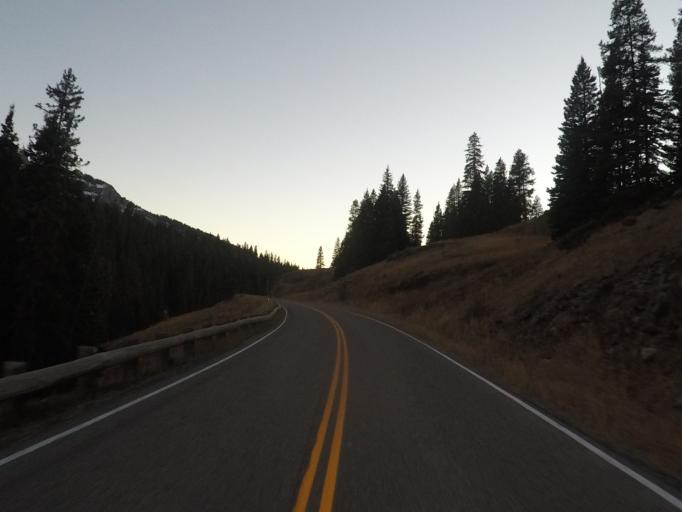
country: US
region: Montana
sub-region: Park County
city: Livingston
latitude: 44.9298
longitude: -110.0864
